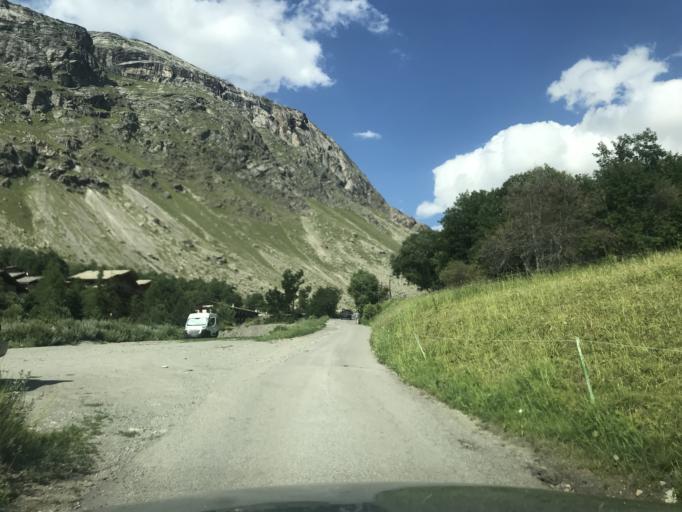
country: FR
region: Rhone-Alpes
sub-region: Departement de la Savoie
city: Val-d'Isere
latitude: 45.3729
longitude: 7.0543
